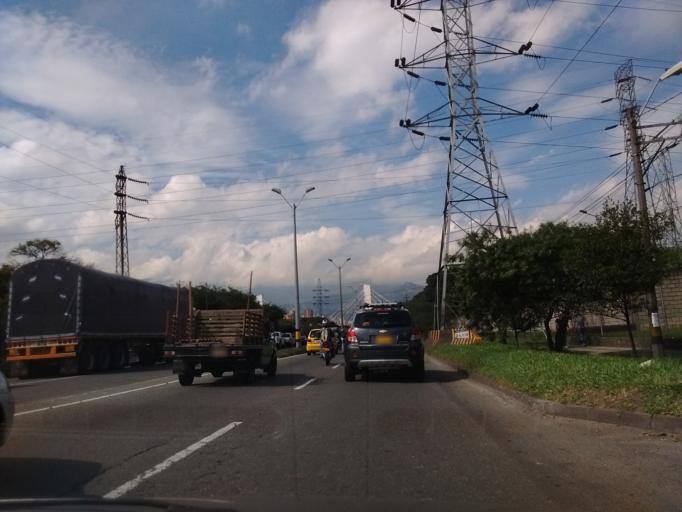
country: CO
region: Antioquia
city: Itagui
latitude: 6.2089
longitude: -75.5791
